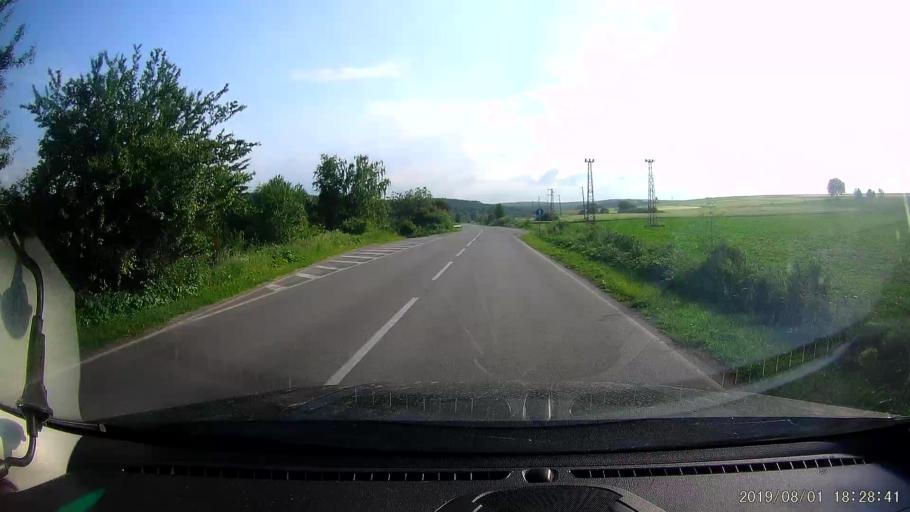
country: BG
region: Shumen
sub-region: Obshtina Venets
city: Venets
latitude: 43.5717
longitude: 26.9594
